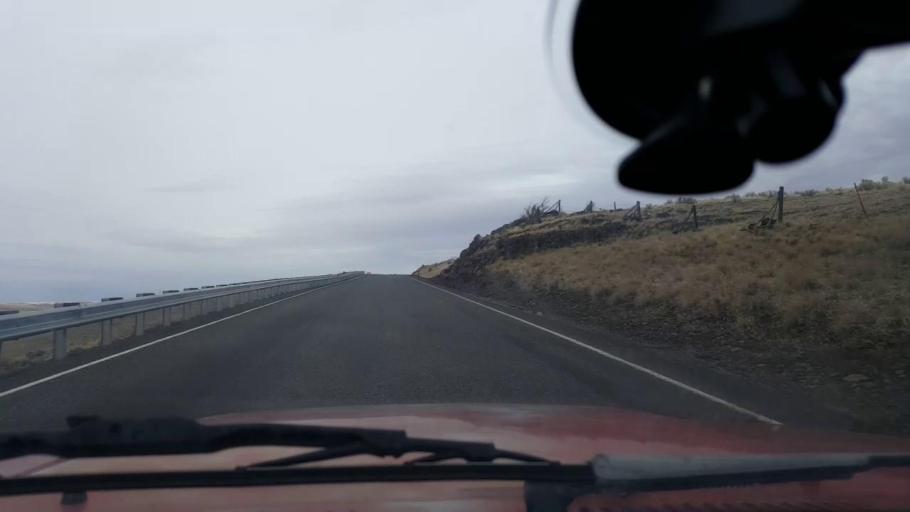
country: US
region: Washington
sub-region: Asotin County
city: Clarkston Heights-Vineland
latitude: 46.3205
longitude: -117.3522
